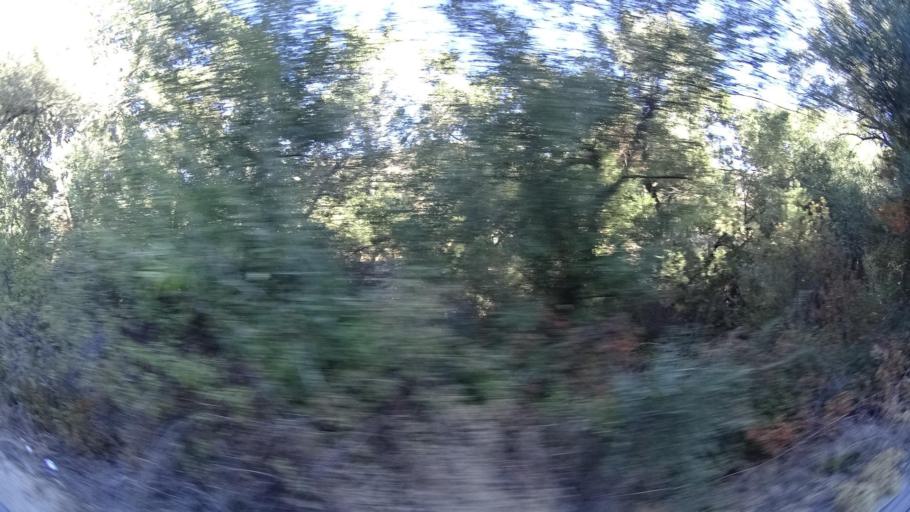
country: MX
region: Baja California
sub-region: Tecate
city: Hacienda Tecate
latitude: 32.5897
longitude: -116.5155
